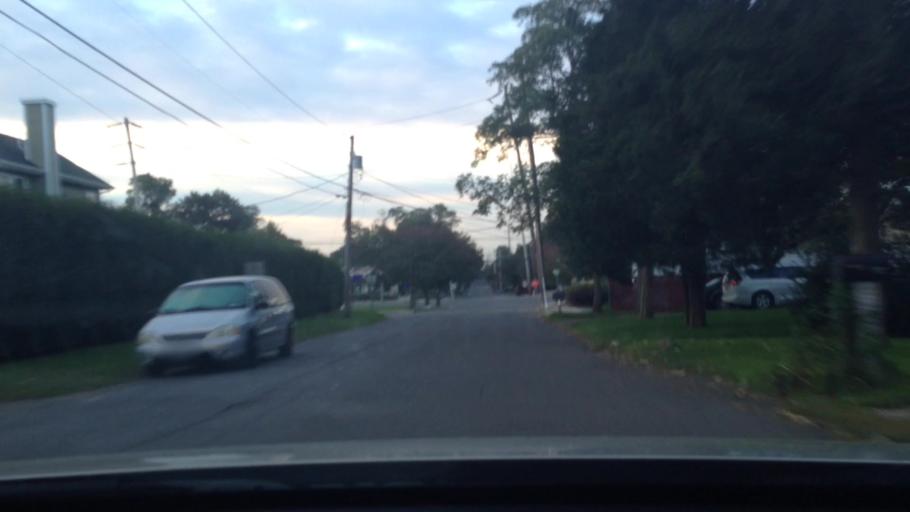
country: US
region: New York
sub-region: Suffolk County
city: Farmingville
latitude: 40.8323
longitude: -73.0286
